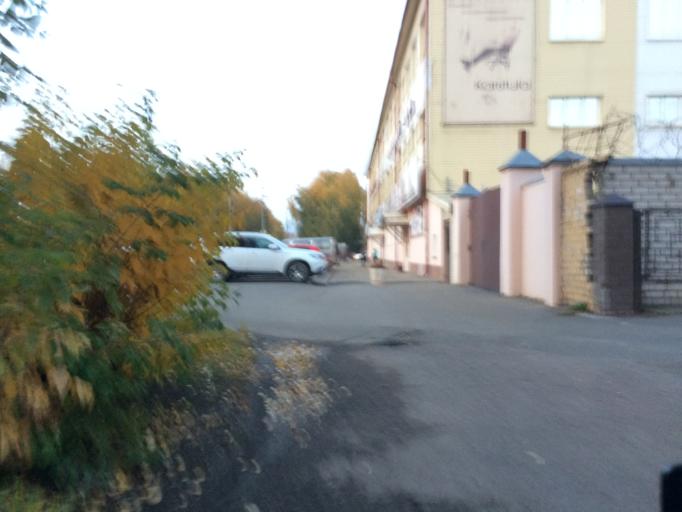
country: RU
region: Mariy-El
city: Yoshkar-Ola
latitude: 56.6157
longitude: 47.8837
